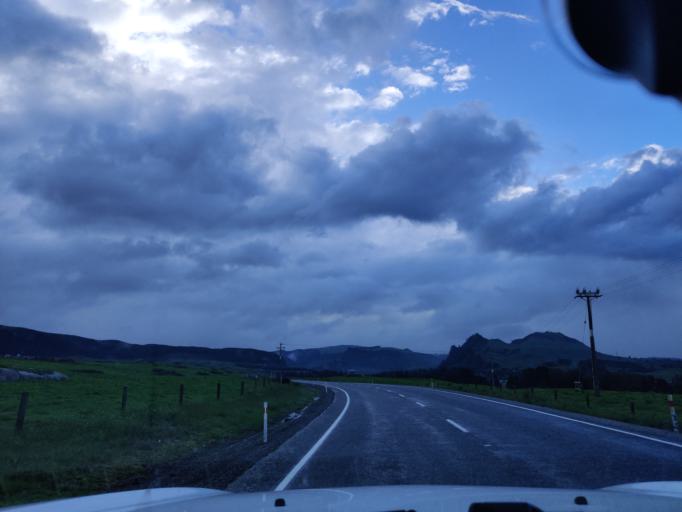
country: NZ
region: Waikato
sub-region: South Waikato District
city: Tokoroa
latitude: -38.4061
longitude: 175.7926
